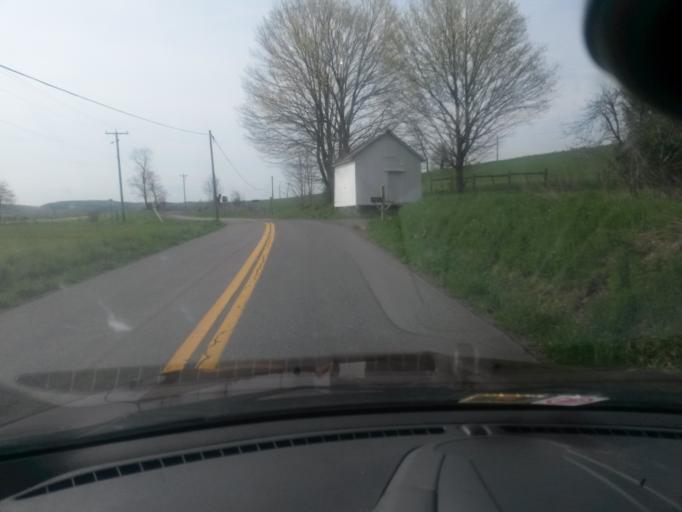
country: US
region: West Virginia
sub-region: Pocahontas County
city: Marlinton
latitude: 38.1199
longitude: -80.2143
